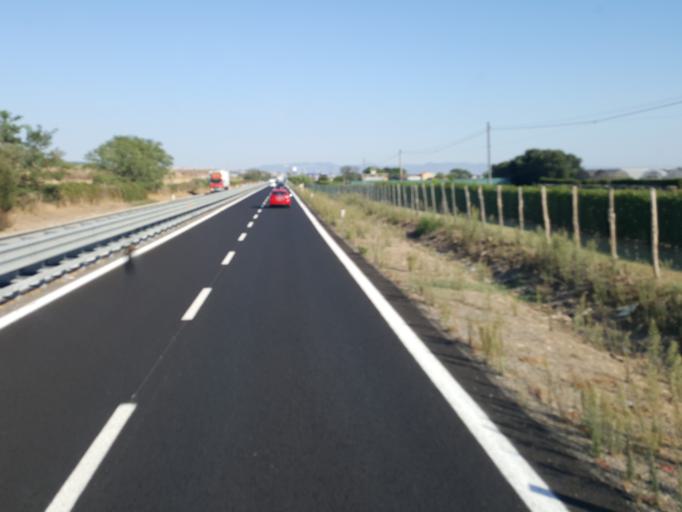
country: IT
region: Latium
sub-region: Provincia di Viterbo
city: Tarquinia
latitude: 42.2758
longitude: 11.7049
